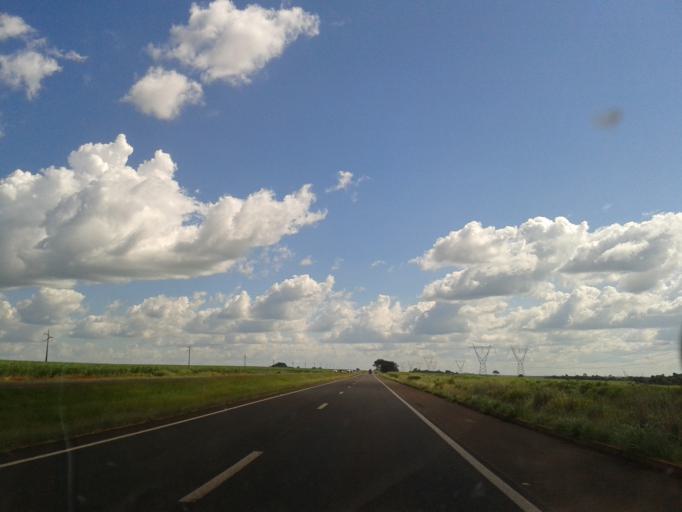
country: BR
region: Goias
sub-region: Goiatuba
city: Goiatuba
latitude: -17.9524
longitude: -49.2496
